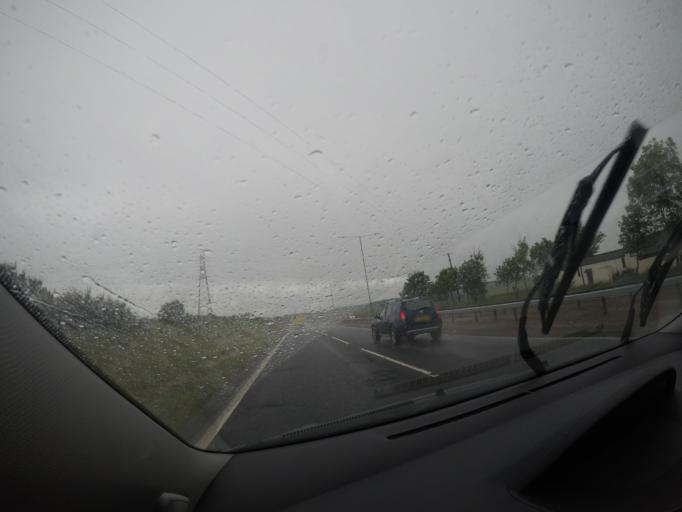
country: GB
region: Scotland
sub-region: Dundee City
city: Dundee
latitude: 56.5213
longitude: -2.9445
